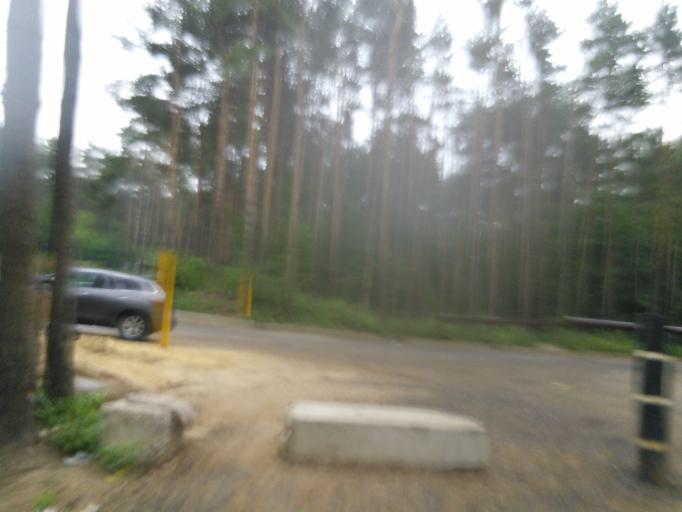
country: RU
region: Moskovskaya
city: Dzerzhinskiy
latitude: 55.6468
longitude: 37.8662
